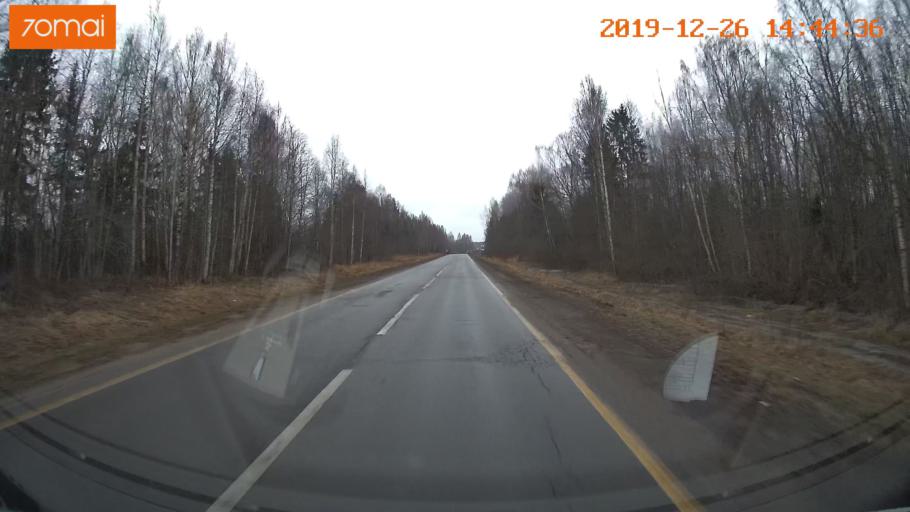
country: RU
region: Jaroslavl
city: Poshekhon'ye
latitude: 58.3459
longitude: 39.0509
